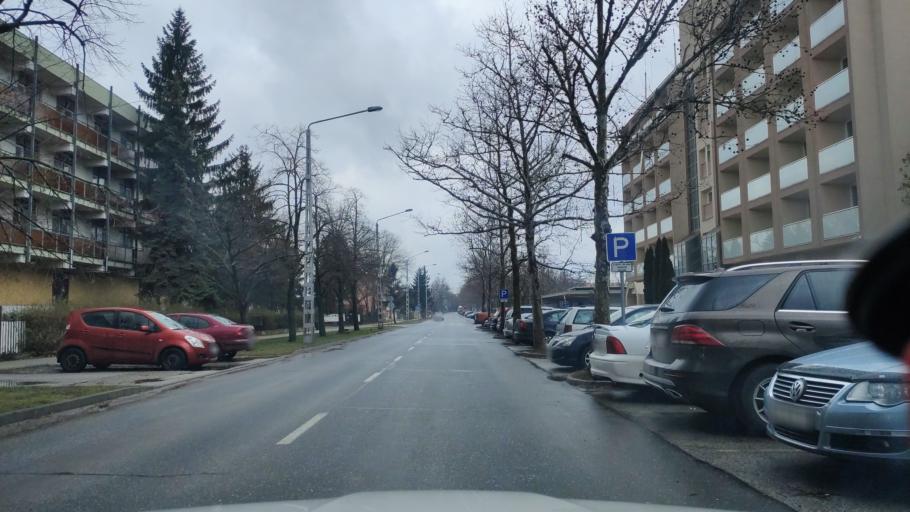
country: HU
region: Hajdu-Bihar
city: Hajduszoboszlo
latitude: 47.4506
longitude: 21.3970
